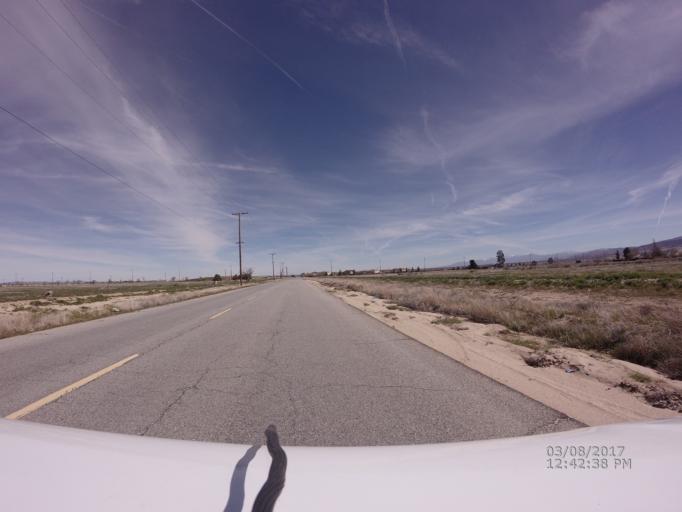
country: US
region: California
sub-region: Los Angeles County
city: Leona Valley
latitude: 34.7038
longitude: -118.2932
